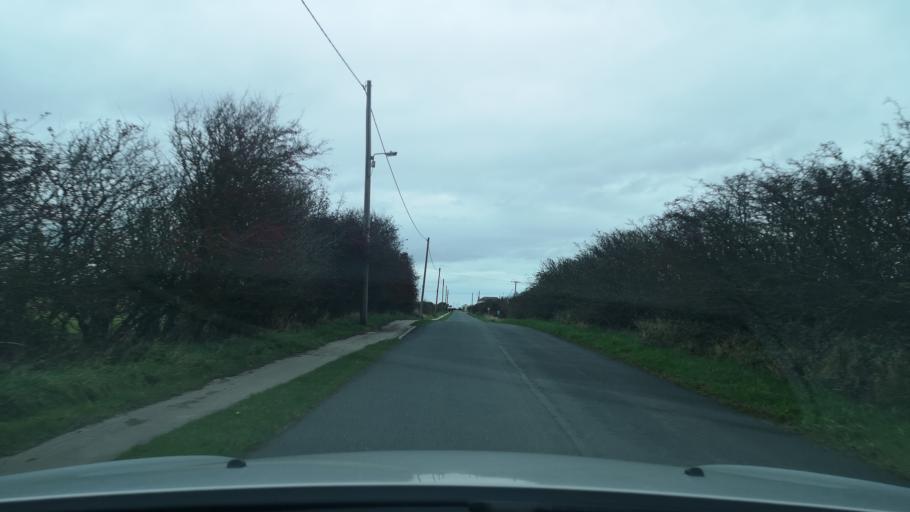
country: GB
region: England
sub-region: East Riding of Yorkshire
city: Easington
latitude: 53.6199
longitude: 0.1350
